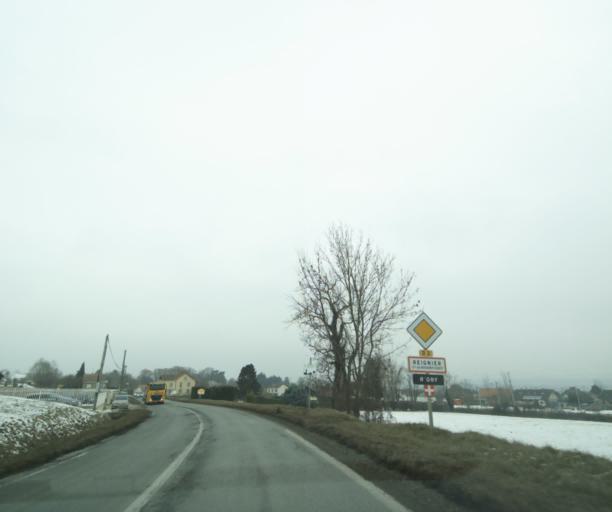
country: FR
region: Rhone-Alpes
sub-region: Departement de la Haute-Savoie
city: Reignier-Esery
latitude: 46.1234
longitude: 6.2684
